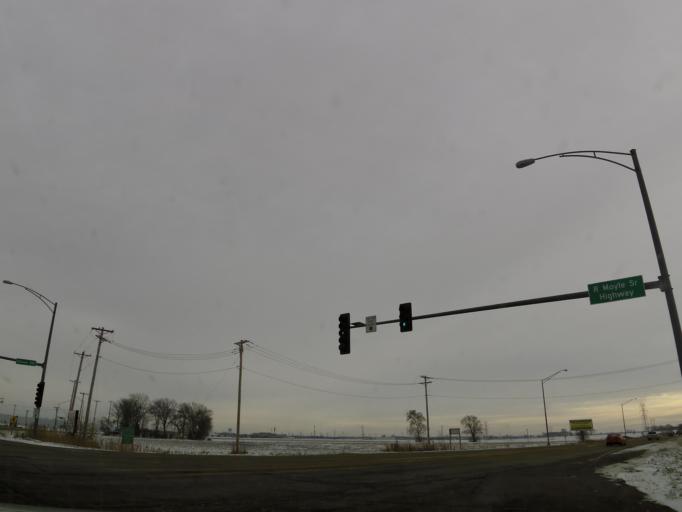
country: US
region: Illinois
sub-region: LaSalle County
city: La Salle
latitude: 41.2947
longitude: -89.1006
